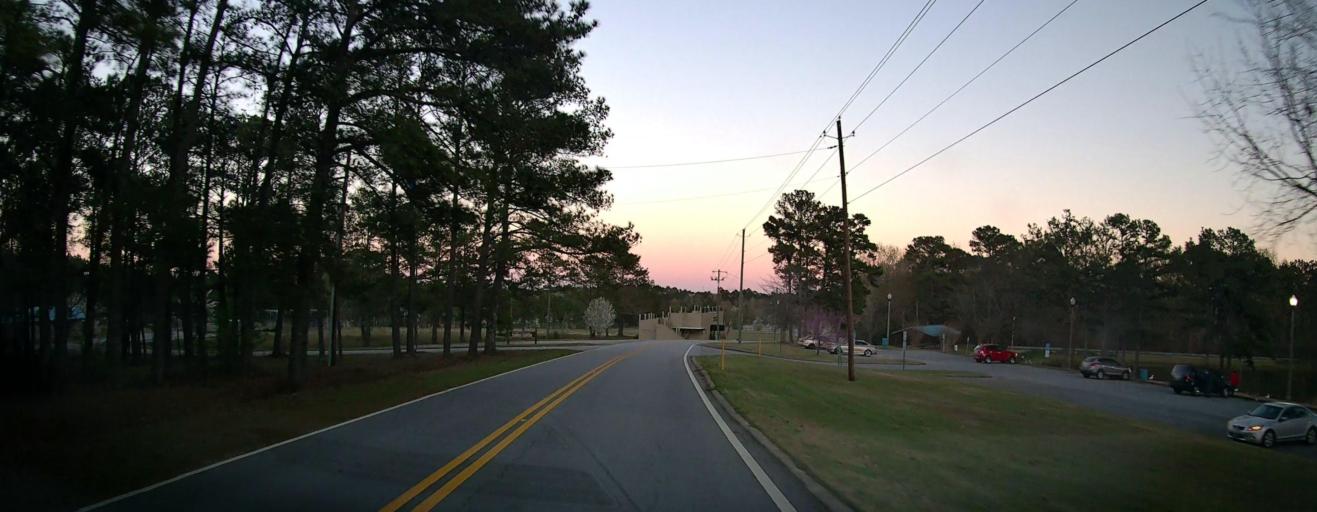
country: US
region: Alabama
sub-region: Russell County
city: Phenix City
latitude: 32.5002
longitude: -85.0087
